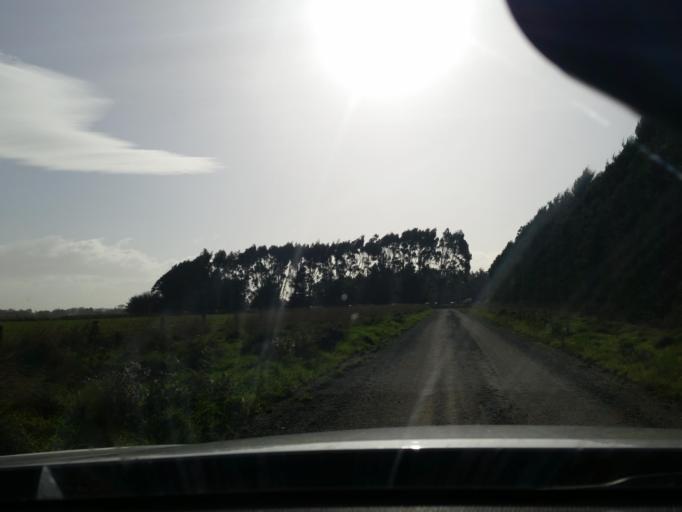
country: NZ
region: Southland
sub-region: Southland District
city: Winton
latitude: -46.2756
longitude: 168.2927
